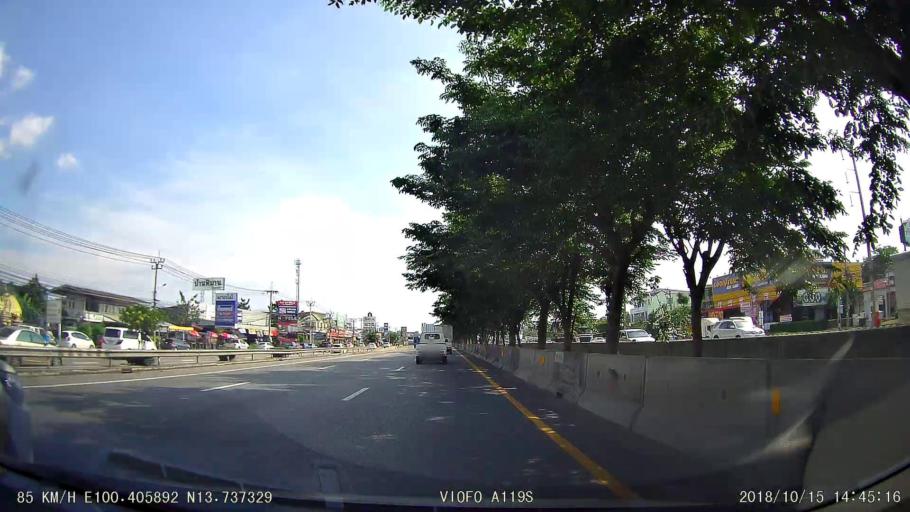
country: TH
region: Bangkok
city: Phasi Charoen
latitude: 13.7369
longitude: 100.4059
